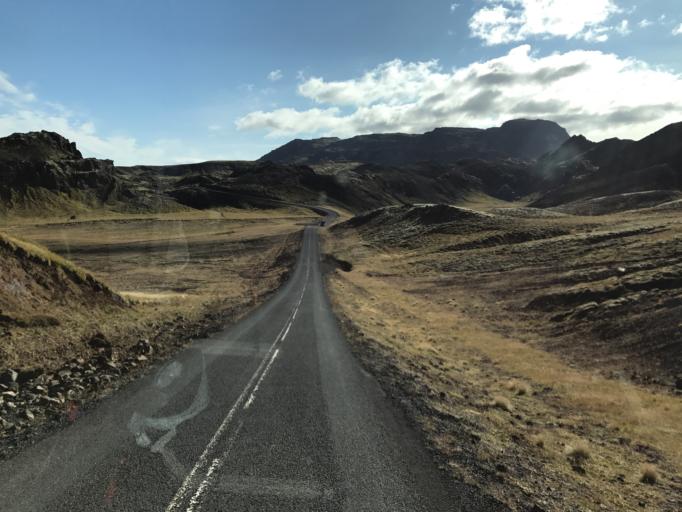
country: IS
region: South
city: Hveragerdi
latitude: 64.1205
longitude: -21.3027
